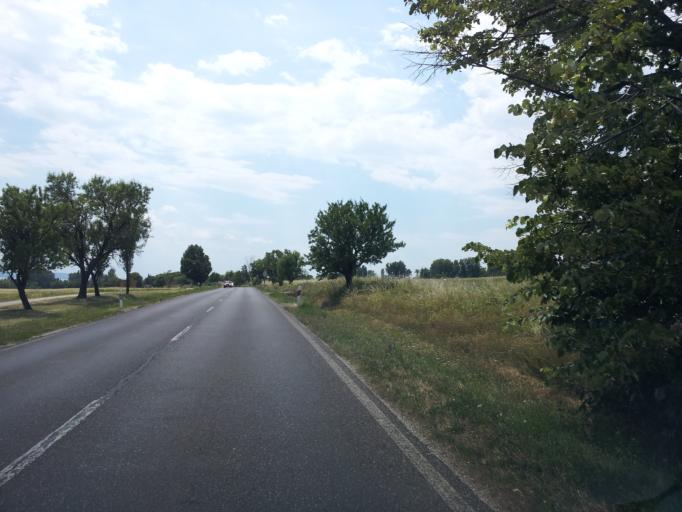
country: HU
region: Veszprem
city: Balatonfured
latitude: 46.9203
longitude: 17.8216
